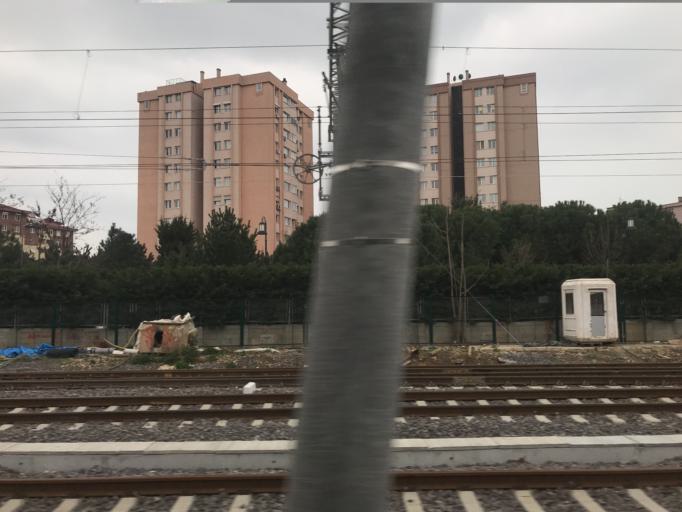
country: TR
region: Istanbul
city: Maltepe
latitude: 40.9190
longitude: 29.1378
